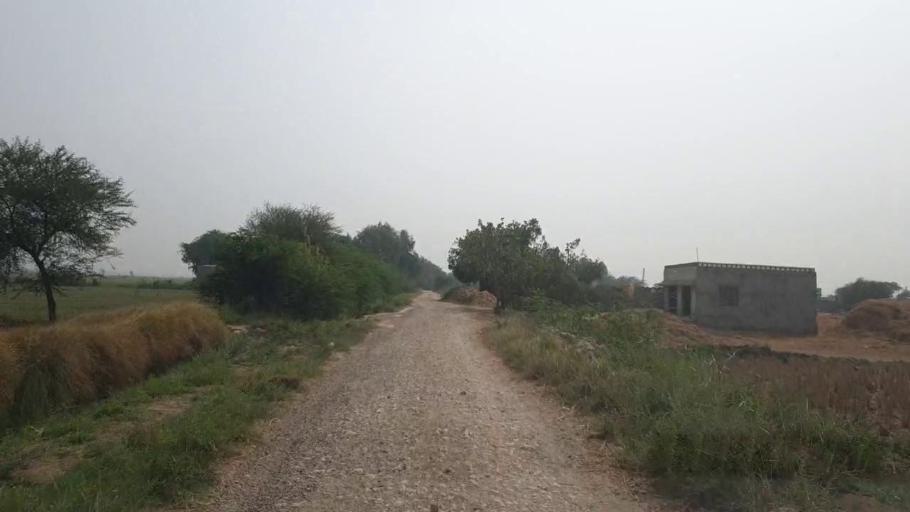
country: PK
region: Sindh
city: Kario
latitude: 24.6509
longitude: 68.6017
